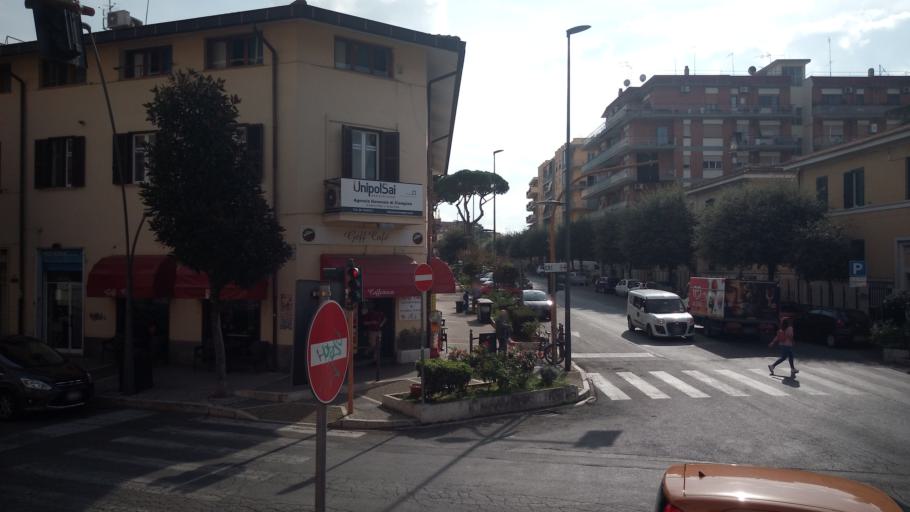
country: IT
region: Latium
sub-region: Citta metropolitana di Roma Capitale
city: Ciampino
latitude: 41.8029
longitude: 12.6002
